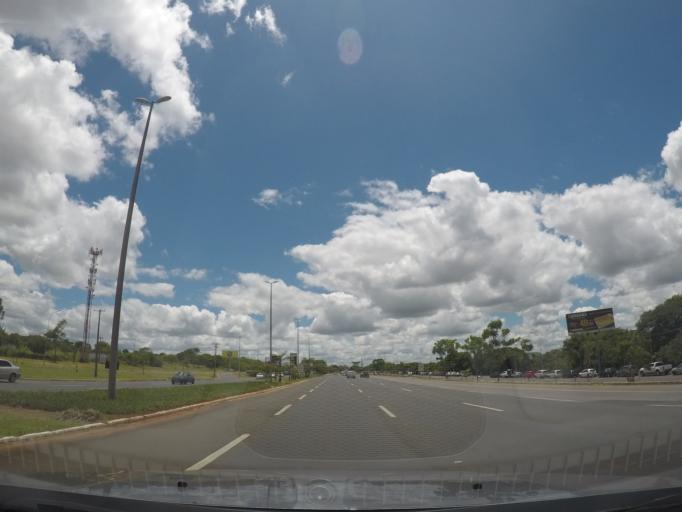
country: BR
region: Federal District
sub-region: Brasilia
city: Brasilia
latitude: -15.8419
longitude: -47.9491
